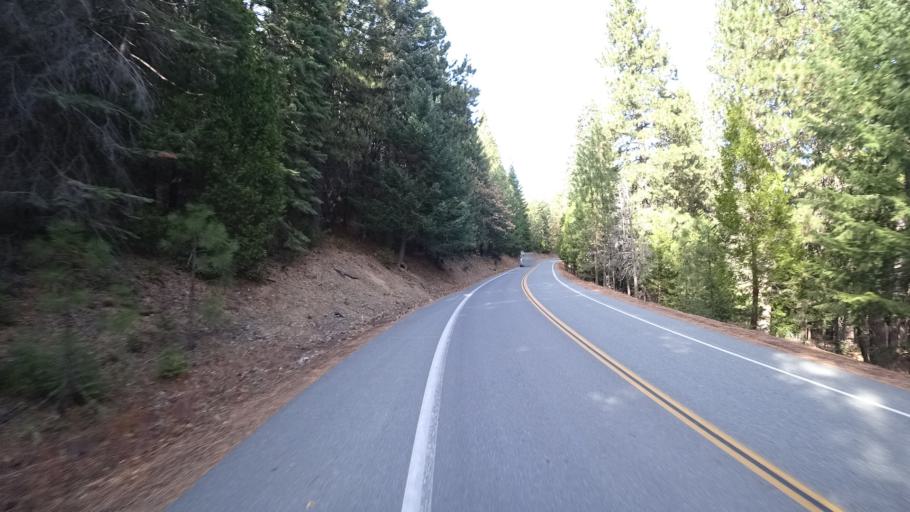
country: US
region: California
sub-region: Siskiyou County
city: Weed
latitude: 41.3791
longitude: -122.3878
